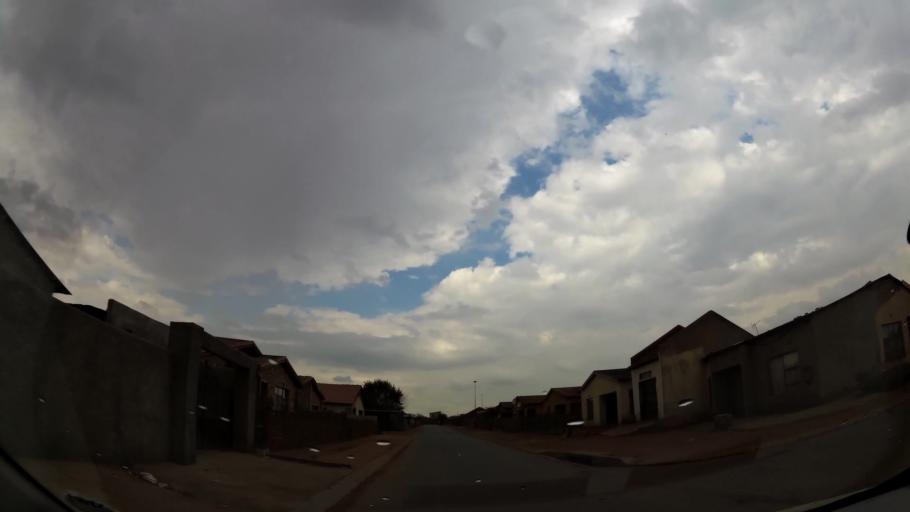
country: ZA
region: Gauteng
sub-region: Ekurhuleni Metropolitan Municipality
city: Germiston
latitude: -26.3635
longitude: 28.1614
